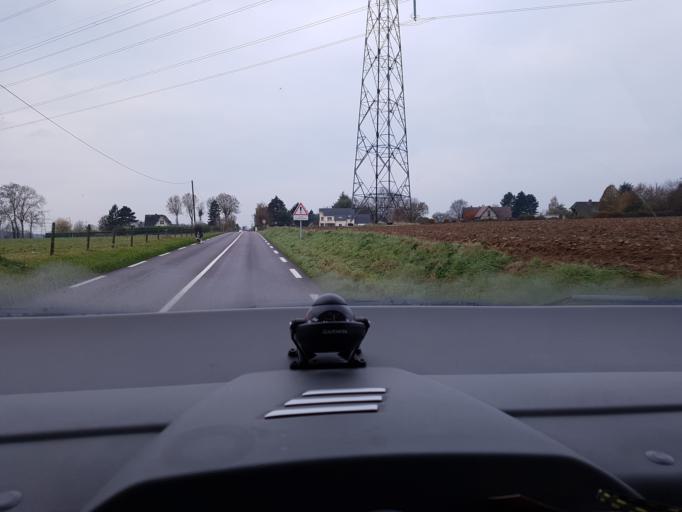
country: FR
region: Haute-Normandie
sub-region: Departement de la Seine-Maritime
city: Roumare
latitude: 49.4997
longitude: 0.9761
